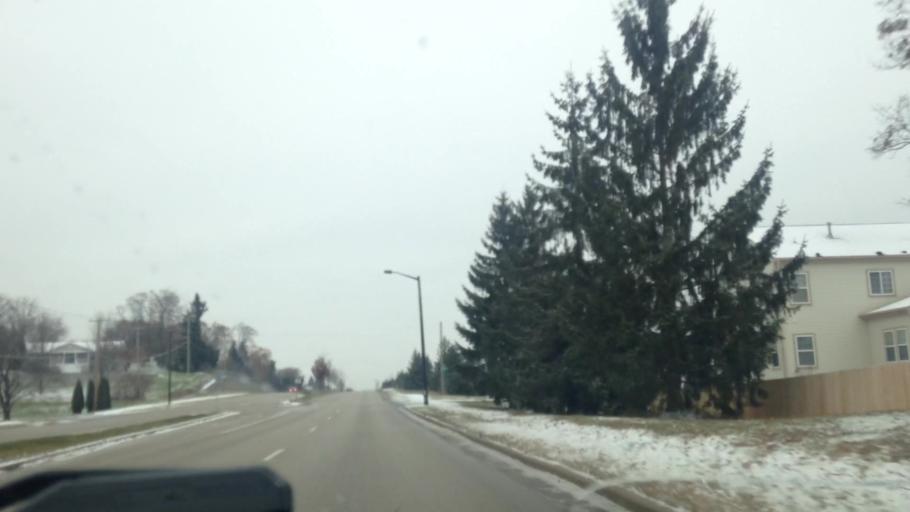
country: US
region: Wisconsin
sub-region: Waukesha County
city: Butler
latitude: 43.1283
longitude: -88.1049
